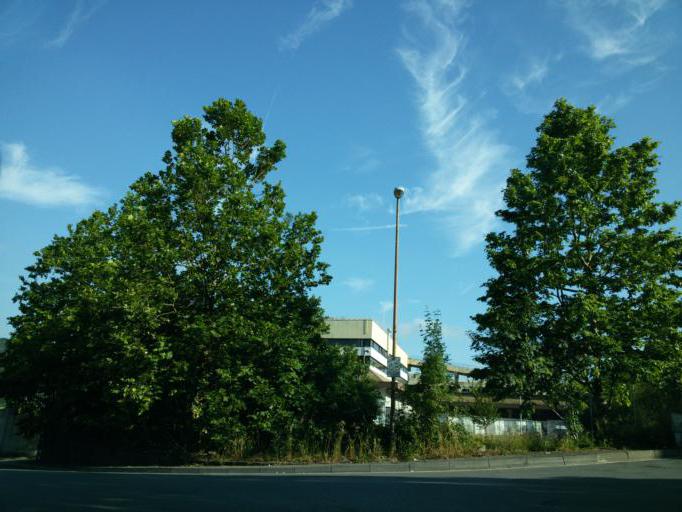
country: IT
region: Liguria
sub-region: Provincia di Genova
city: Manesseno
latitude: 44.4699
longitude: 8.8967
